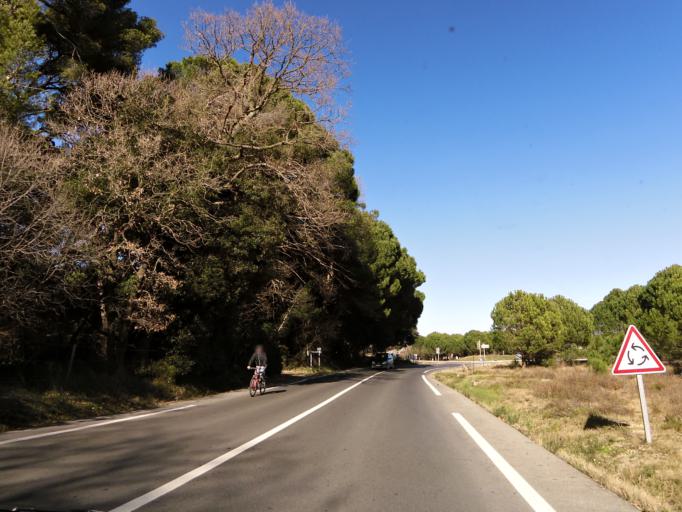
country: FR
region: Languedoc-Roussillon
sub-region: Departement du Gard
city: Aigues-Mortes
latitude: 43.5846
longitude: 4.2089
